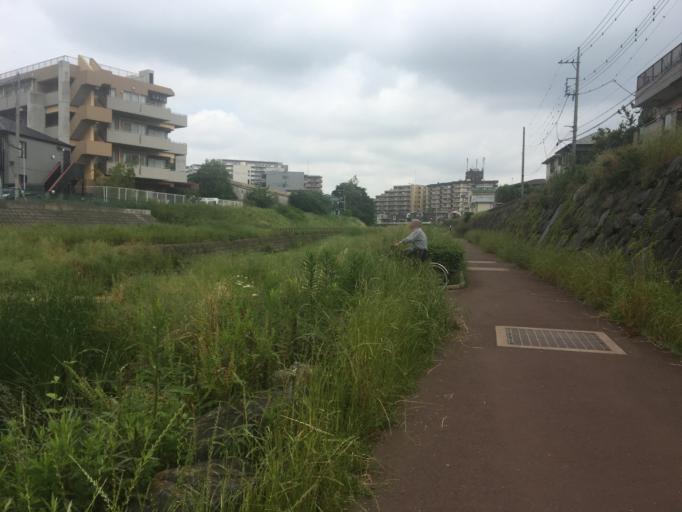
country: JP
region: Saitama
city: Kawaguchi
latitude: 35.8125
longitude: 139.7298
